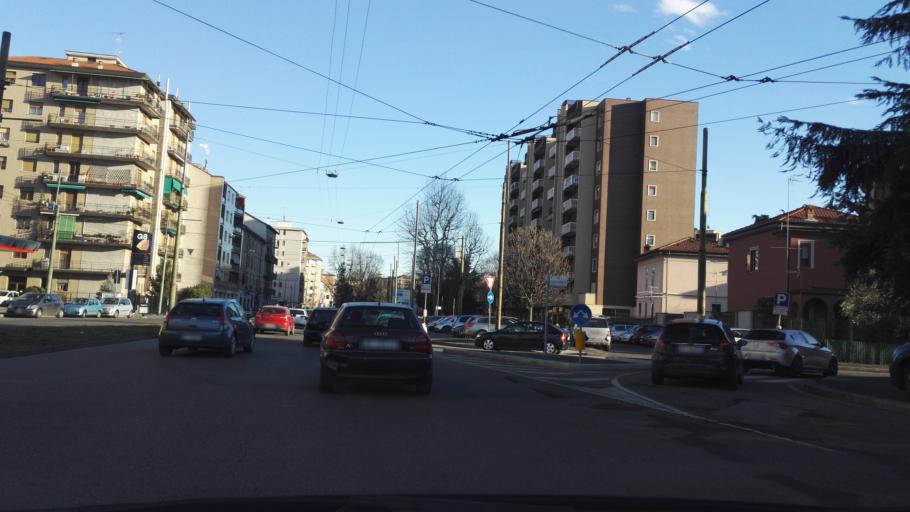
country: IT
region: Lombardy
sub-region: Citta metropolitana di Milano
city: Romano Banco
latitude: 45.4699
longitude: 9.1238
